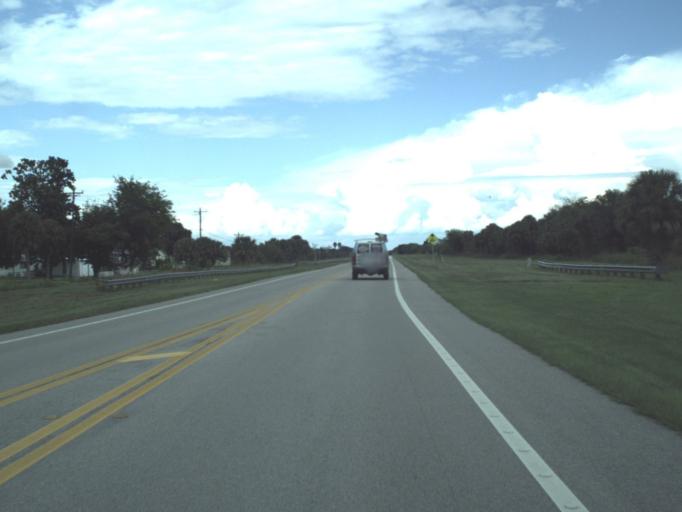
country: US
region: Florida
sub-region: Glades County
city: Moore Haven
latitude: 26.9864
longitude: -81.0975
